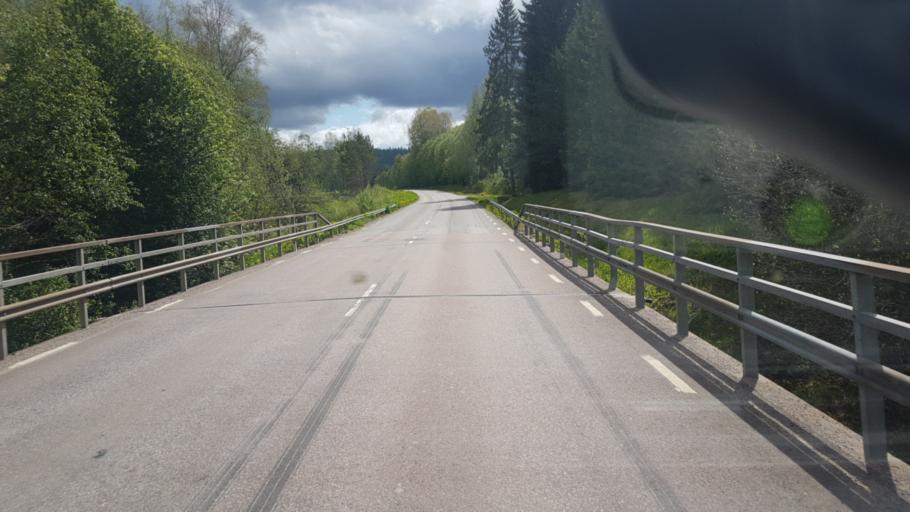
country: SE
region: Vaermland
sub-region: Eda Kommun
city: Amotfors
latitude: 59.6815
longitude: 12.1207
